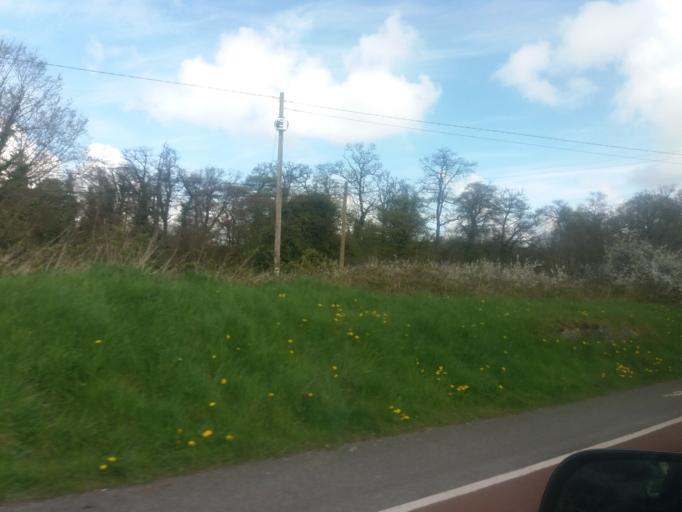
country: IE
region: Ulster
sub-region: An Cabhan
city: Cavan
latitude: 54.0069
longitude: -7.3476
